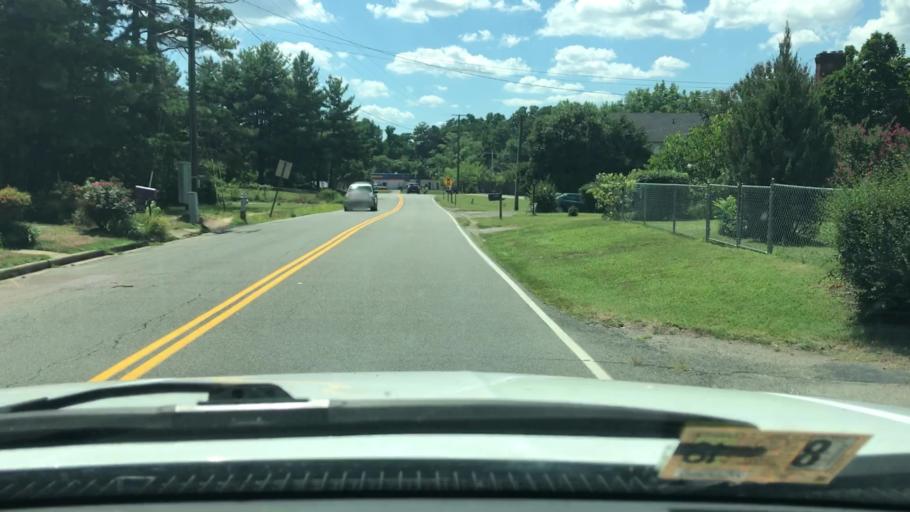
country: US
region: Virginia
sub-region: Henrico County
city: East Highland Park
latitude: 37.5700
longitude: -77.3987
